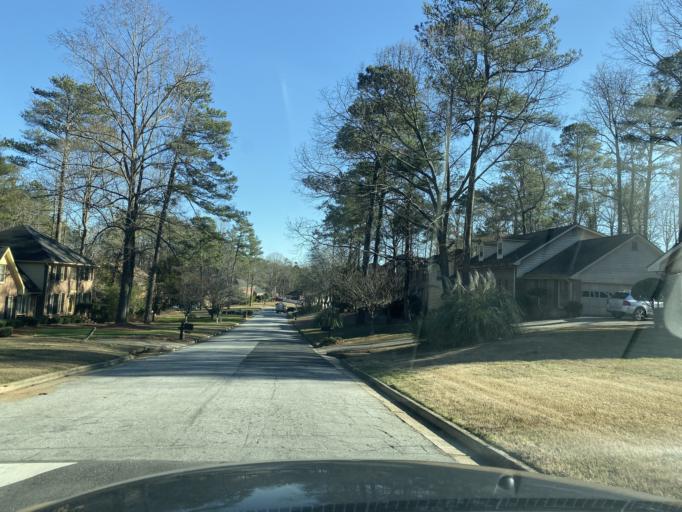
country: US
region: Georgia
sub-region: DeKalb County
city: Pine Mountain
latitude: 33.6811
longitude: -84.1589
